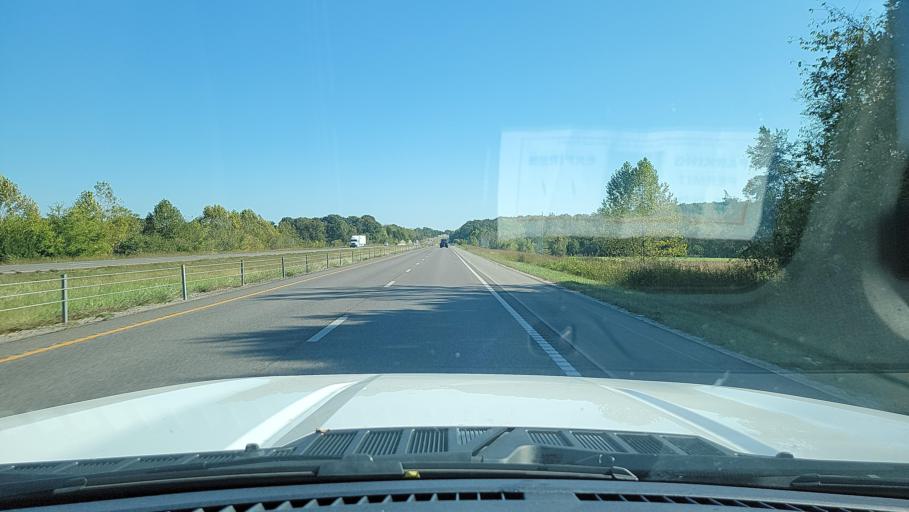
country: US
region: Missouri
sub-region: Sainte Genevieve County
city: Sainte Genevieve
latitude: 37.9972
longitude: -90.2126
